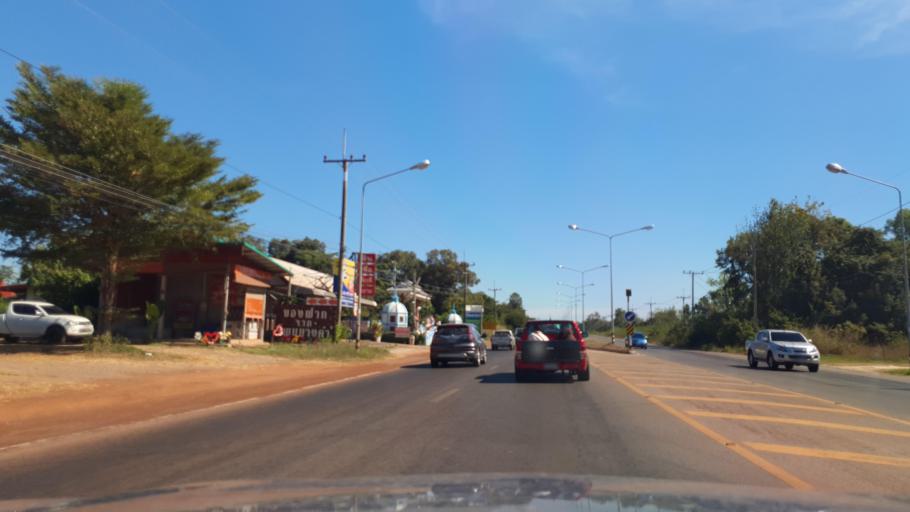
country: TH
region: Sakon Nakhon
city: Tao Ngoi
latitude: 17.0815
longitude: 104.1936
